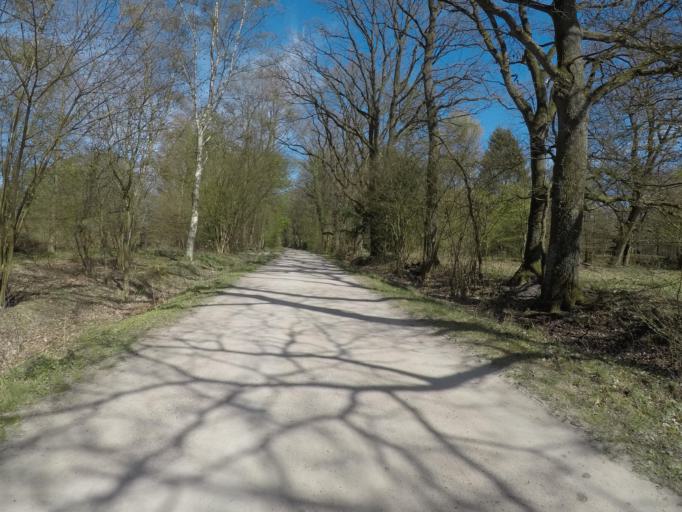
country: DE
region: Hamburg
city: Wohldorf-Ohlstedt
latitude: 53.7202
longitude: 10.1670
